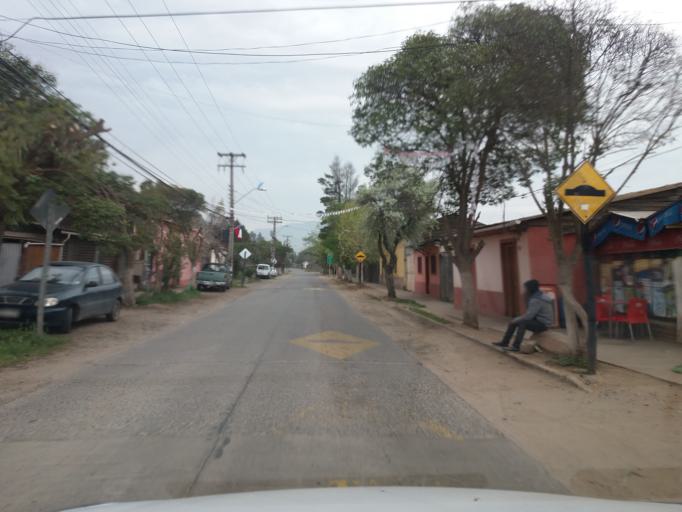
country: CL
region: Valparaiso
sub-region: Provincia de Quillota
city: Hacienda La Calera
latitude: -32.8212
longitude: -71.1324
